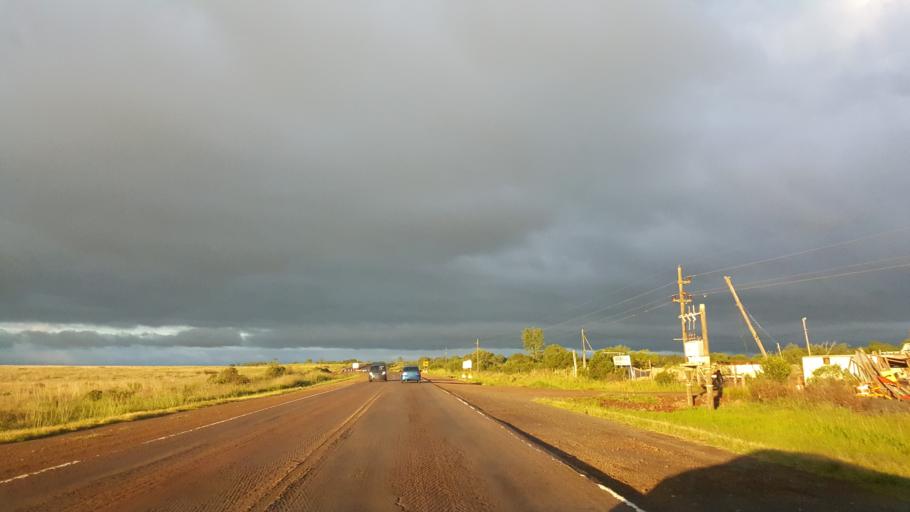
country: AR
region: Misiones
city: Cerro Cora
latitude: -27.4385
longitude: -55.6435
